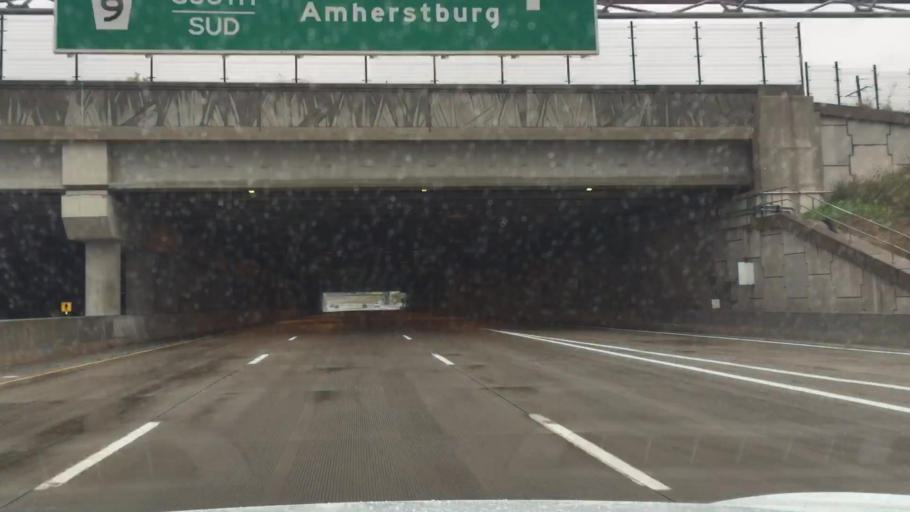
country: CA
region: Ontario
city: Windsor
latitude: 42.2367
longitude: -83.0008
